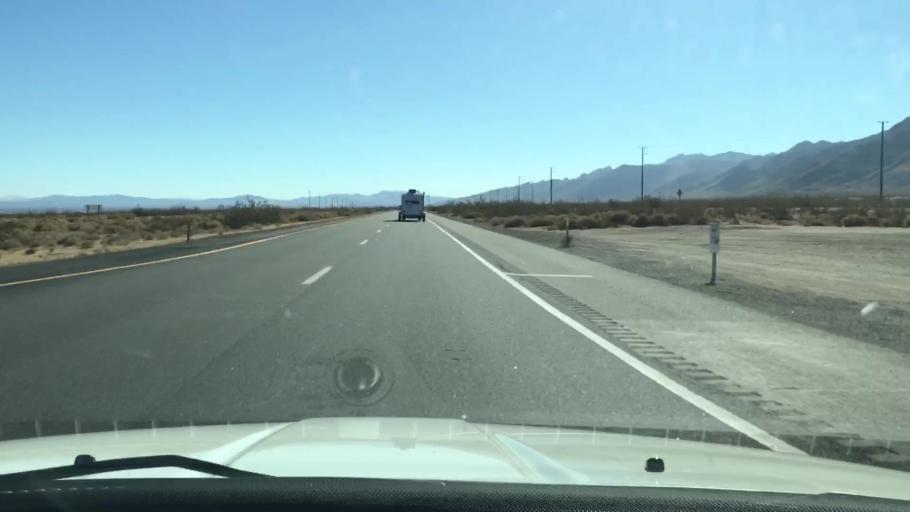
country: US
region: California
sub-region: Kern County
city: Inyokern
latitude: 35.8418
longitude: -117.8752
